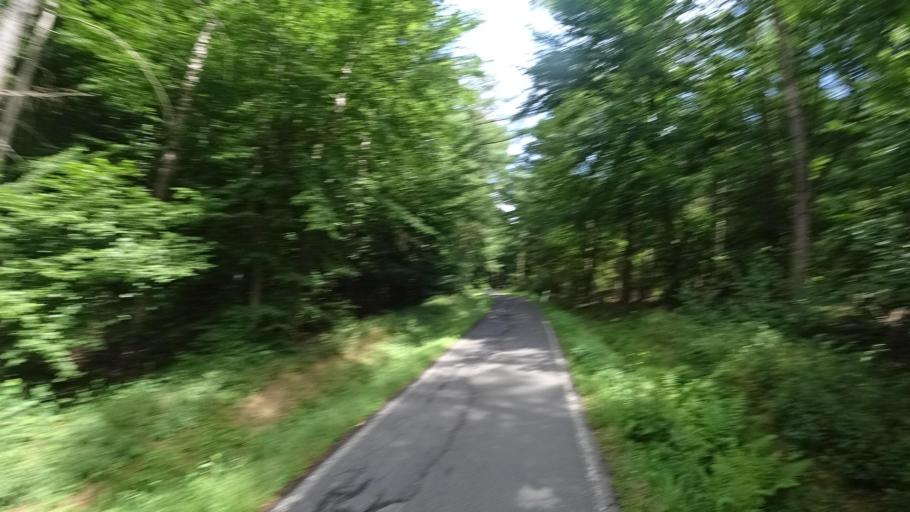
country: DE
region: Rheinland-Pfalz
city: Ratzert
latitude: 50.6567
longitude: 7.6231
